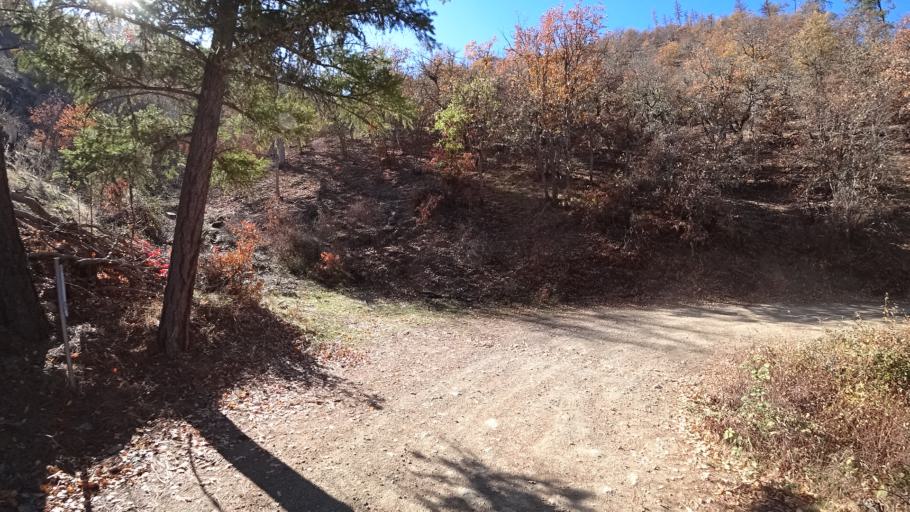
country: US
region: California
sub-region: Siskiyou County
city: Yreka
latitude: 41.8612
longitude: -122.7222
